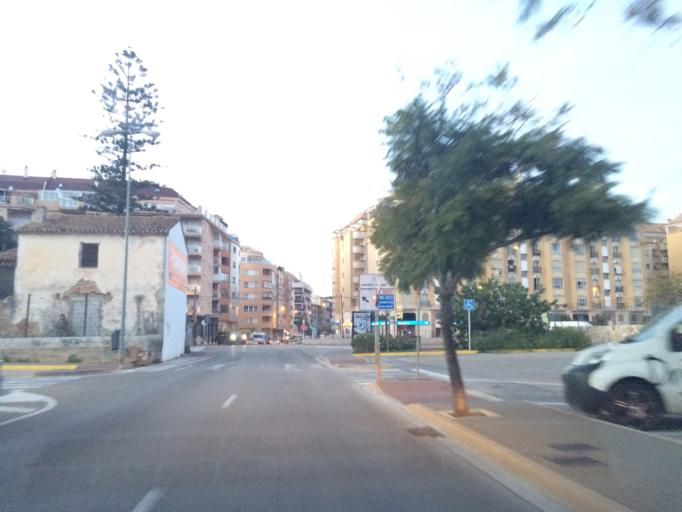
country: ES
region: Valencia
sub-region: Provincia de Alicante
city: Denia
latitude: 38.8351
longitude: 0.1095
